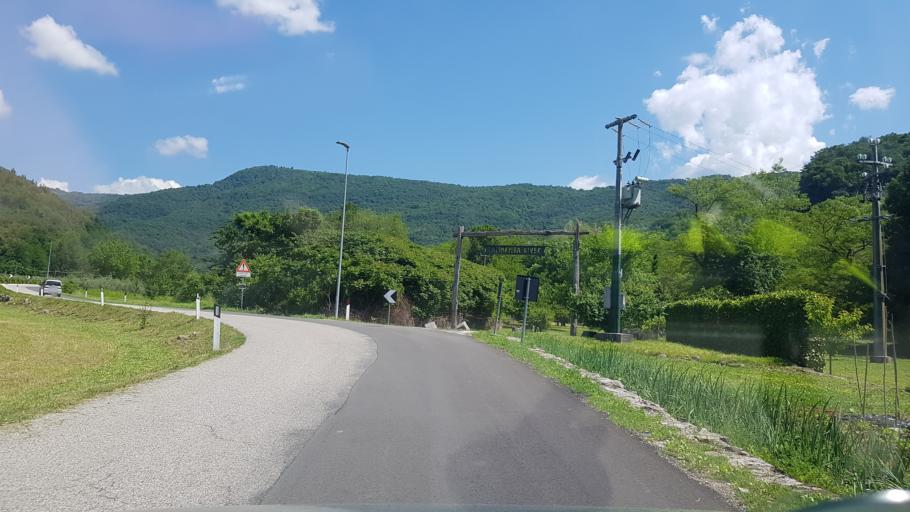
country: IT
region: Friuli Venezia Giulia
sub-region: Provincia di Udine
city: Torreano
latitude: 46.1350
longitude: 13.4381
